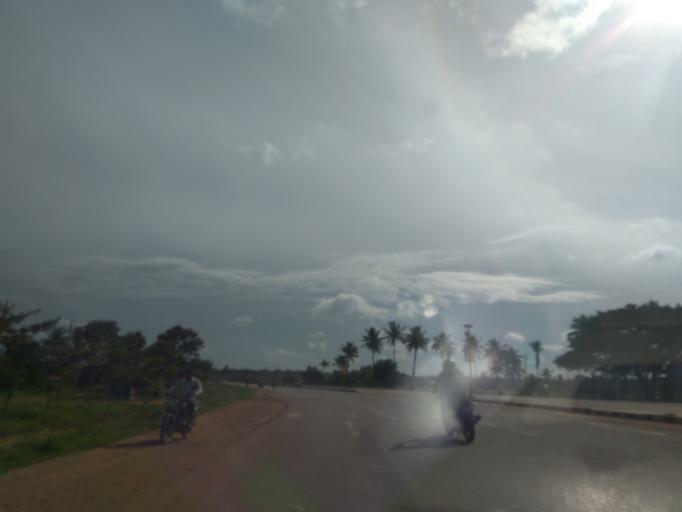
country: IN
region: Karnataka
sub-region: Bangalore Rural
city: Dasarahalli
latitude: 13.0849
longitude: 77.8249
